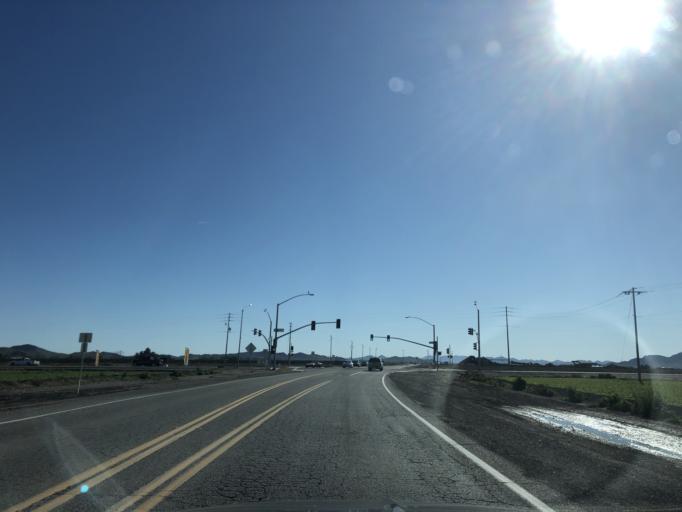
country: US
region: Arizona
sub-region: Maricopa County
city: Buckeye
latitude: 33.3785
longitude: -112.4778
